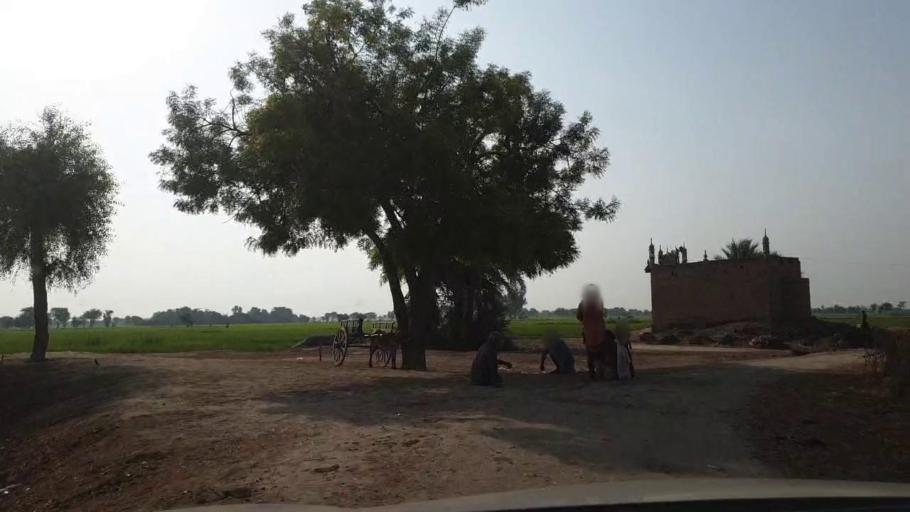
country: PK
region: Sindh
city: Larkana
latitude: 27.4923
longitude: 68.2117
